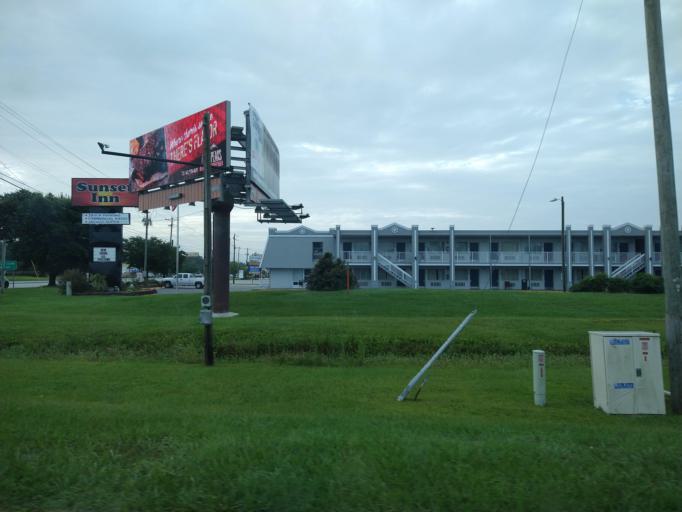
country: US
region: North Carolina
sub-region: Onslow County
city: Pumpkin Center
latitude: 34.7768
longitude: -77.3930
